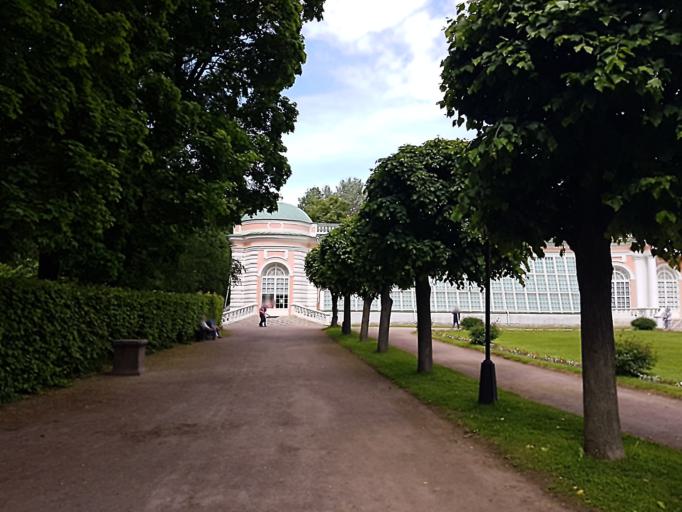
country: RU
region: Moskovskaya
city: Kuskovo
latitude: 55.7380
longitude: 37.8094
